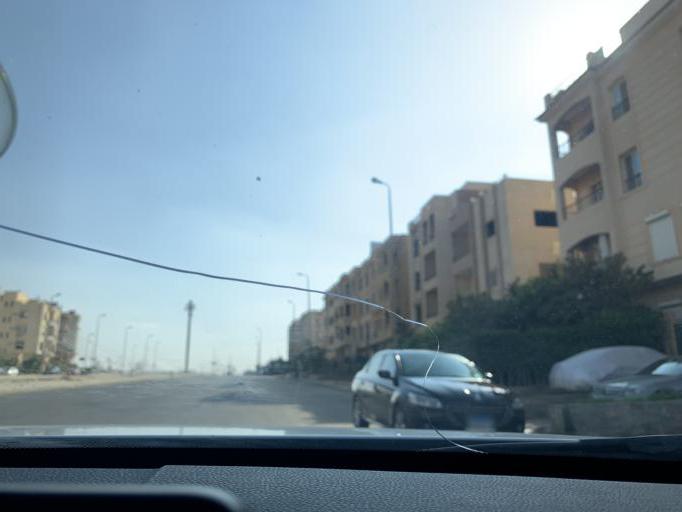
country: EG
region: Muhafazat al Qalyubiyah
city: Al Khankah
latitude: 30.0023
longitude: 31.4804
